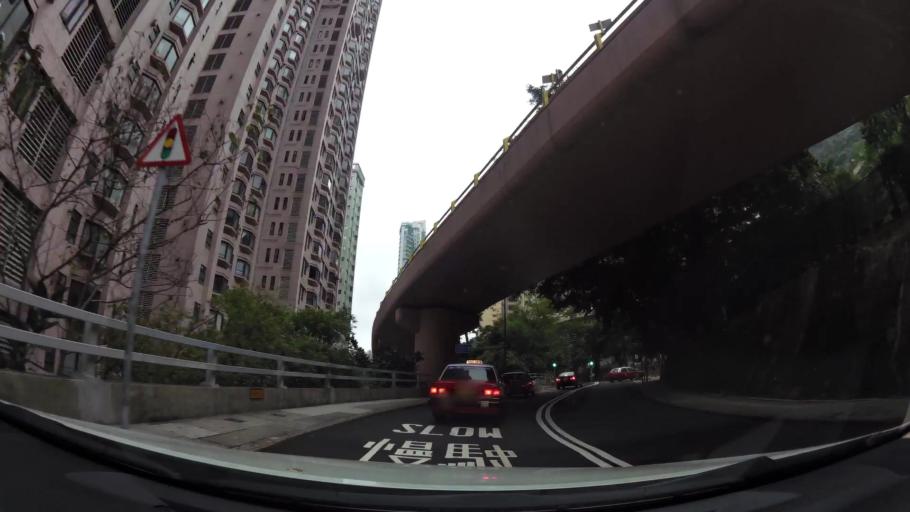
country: HK
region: Central and Western
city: Central
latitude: 22.2750
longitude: 114.1556
